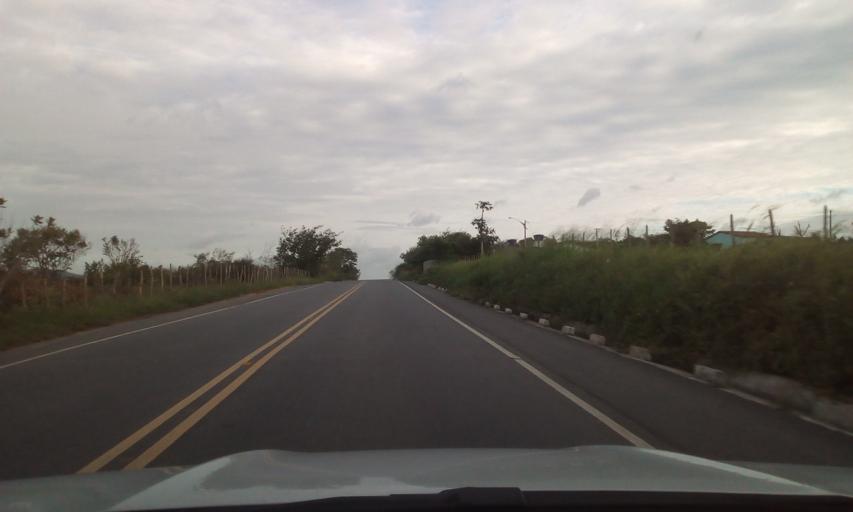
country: BR
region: Paraiba
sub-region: Serra Redonda
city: Alagoa Grande
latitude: -7.2095
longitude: -35.5925
